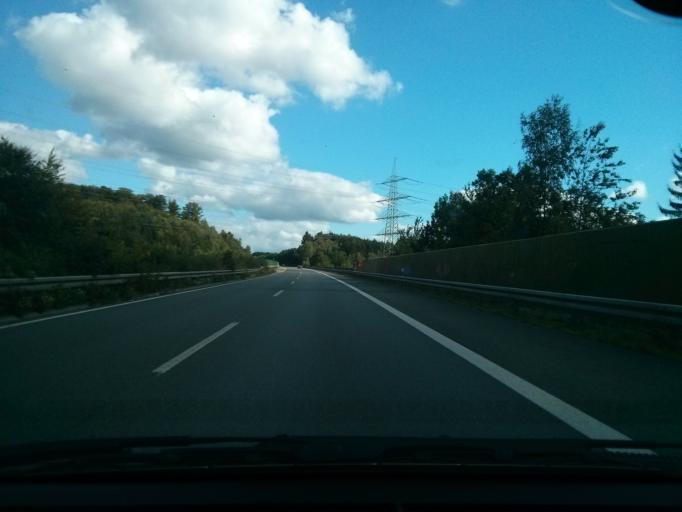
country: DE
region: North Rhine-Westphalia
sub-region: Regierungsbezirk Arnsberg
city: Arnsberg
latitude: 51.4333
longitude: 8.0099
